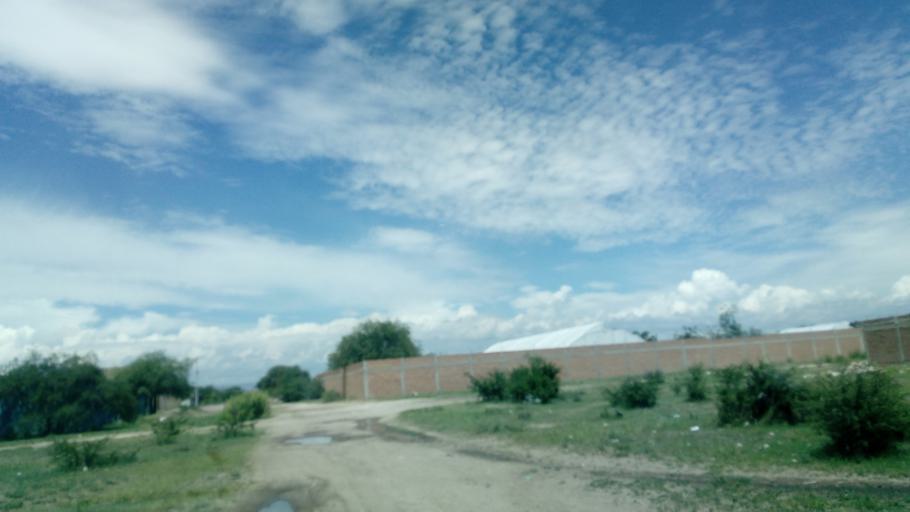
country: MX
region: Durango
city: Victoria de Durango
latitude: 24.0147
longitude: -104.5883
